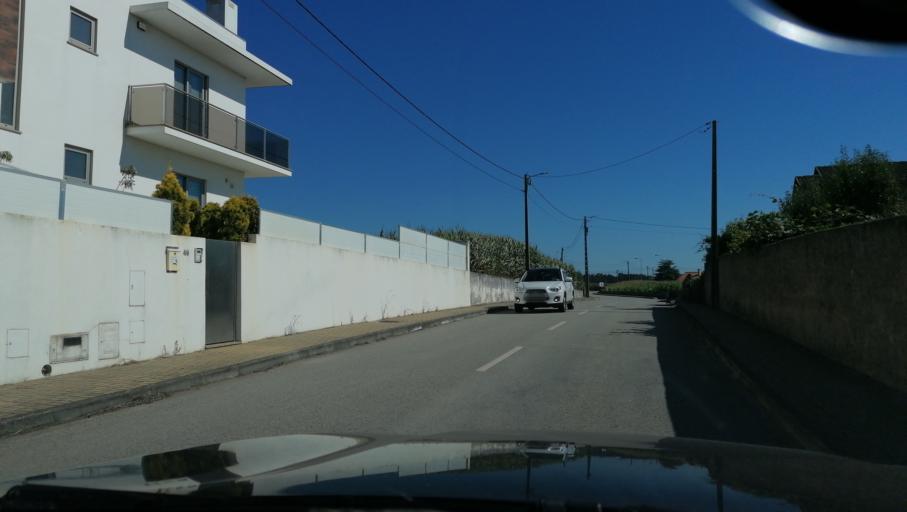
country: PT
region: Aveiro
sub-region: Estarreja
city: Salreu
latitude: 40.7447
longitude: -8.5464
